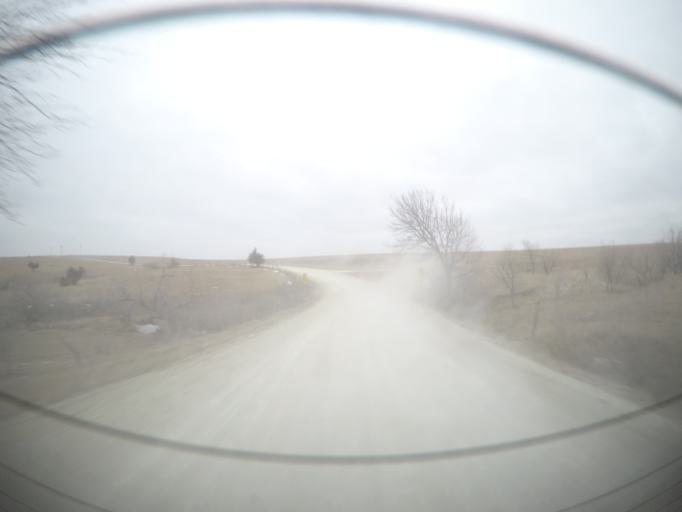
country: US
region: Kansas
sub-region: Pottawatomie County
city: Wamego
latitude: 39.1300
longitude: -96.2418
